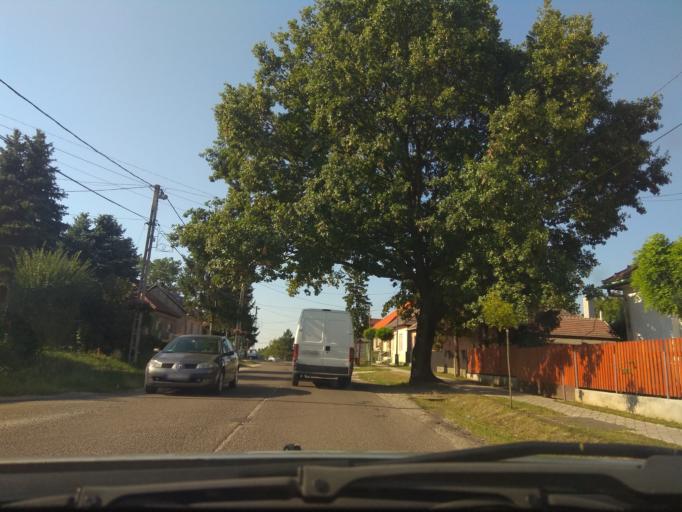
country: HU
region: Borsod-Abauj-Zemplen
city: Emod
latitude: 47.9370
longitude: 20.8169
